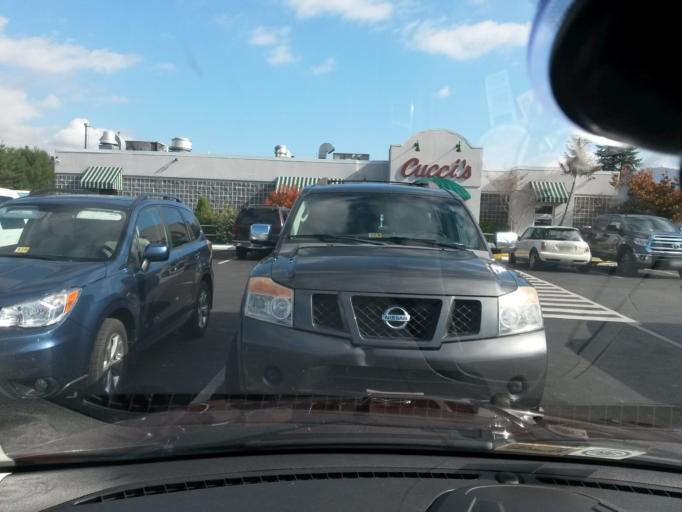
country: US
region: Virginia
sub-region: City of Covington
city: Fairlawn
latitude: 37.7785
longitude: -79.9785
